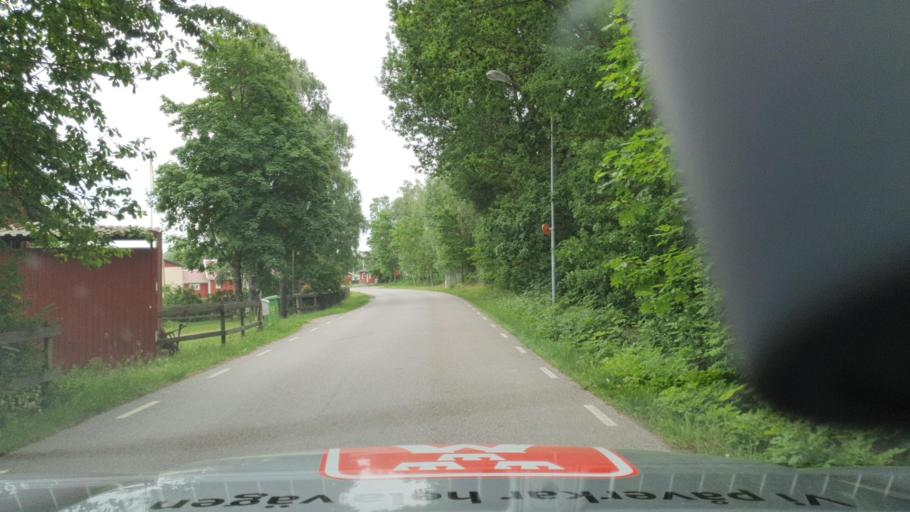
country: SE
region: Kalmar
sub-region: Kalmar Kommun
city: Trekanten
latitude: 56.6202
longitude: 16.0463
